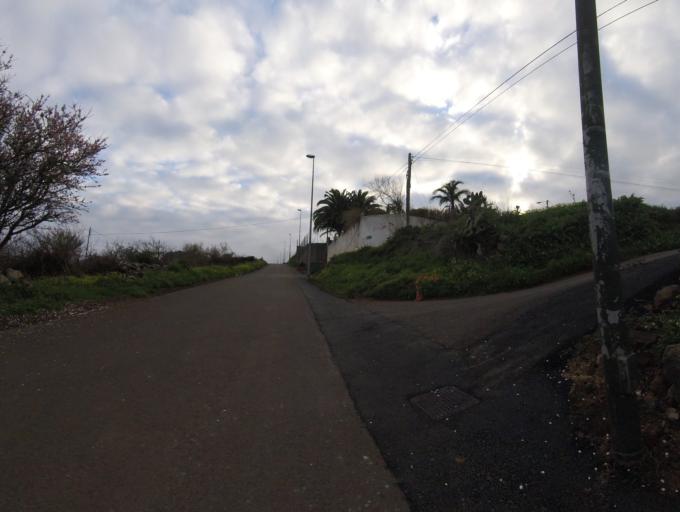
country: ES
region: Canary Islands
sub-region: Provincia de Santa Cruz de Tenerife
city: La Laguna
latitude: 28.4521
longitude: -16.3524
